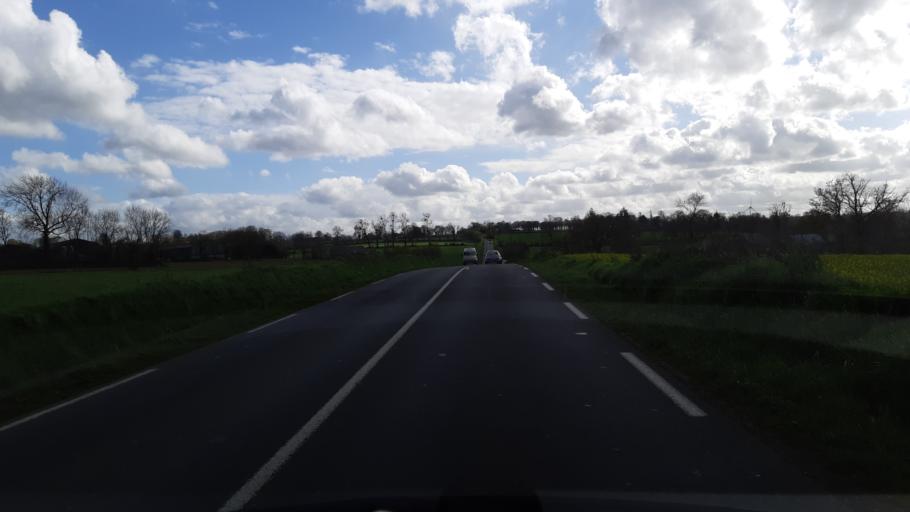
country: FR
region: Lower Normandy
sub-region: Departement de la Manche
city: Agneaux
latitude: 49.0391
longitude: -1.1319
